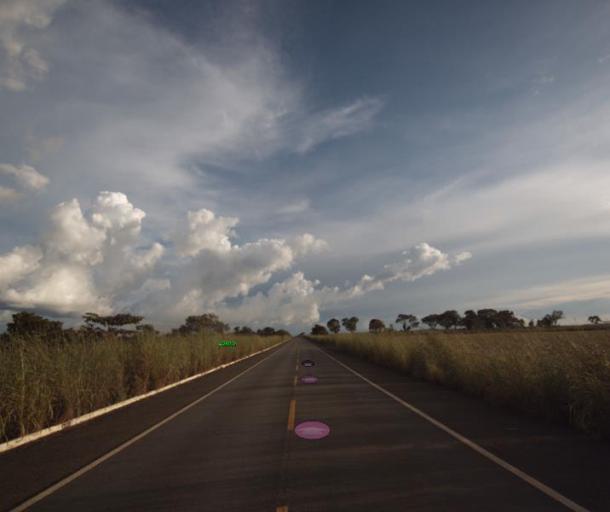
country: BR
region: Goias
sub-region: Niquelandia
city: Niquelandia
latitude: -14.7427
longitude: -48.6177
